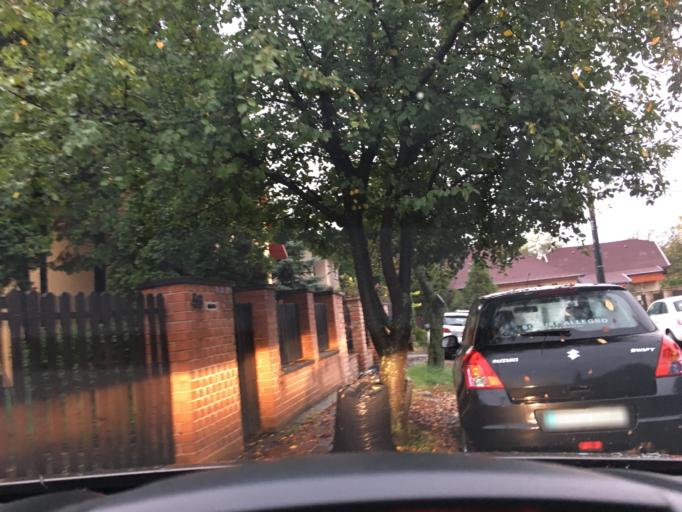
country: HU
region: Budapest
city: Budapest XVI. keruelet
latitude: 47.5003
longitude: 19.1894
